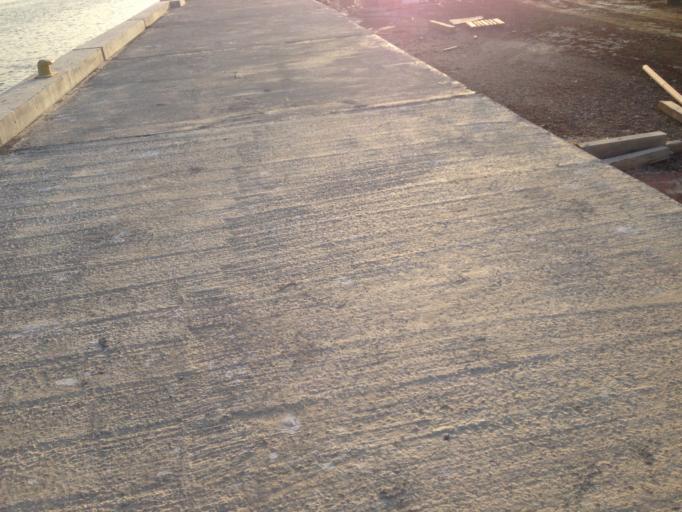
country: OM
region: Muhafazat Masqat
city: As Sib al Jadidah
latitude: 23.6326
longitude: 58.2701
